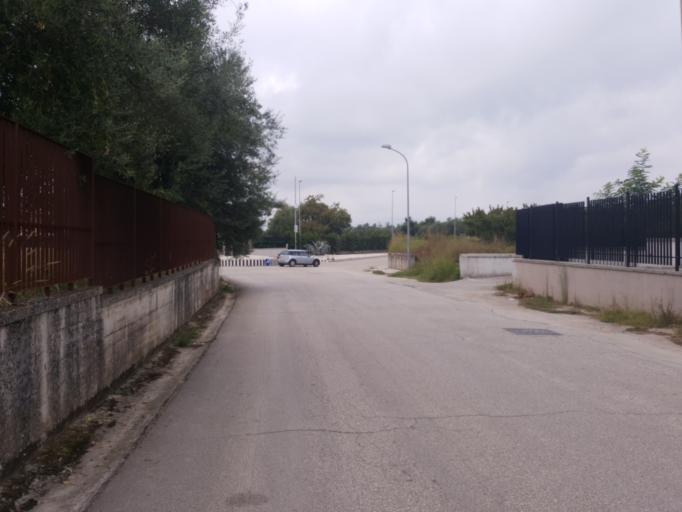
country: IT
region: Campania
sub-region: Provincia di Caserta
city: Pignataro Maggiore
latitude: 41.1889
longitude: 14.1652
